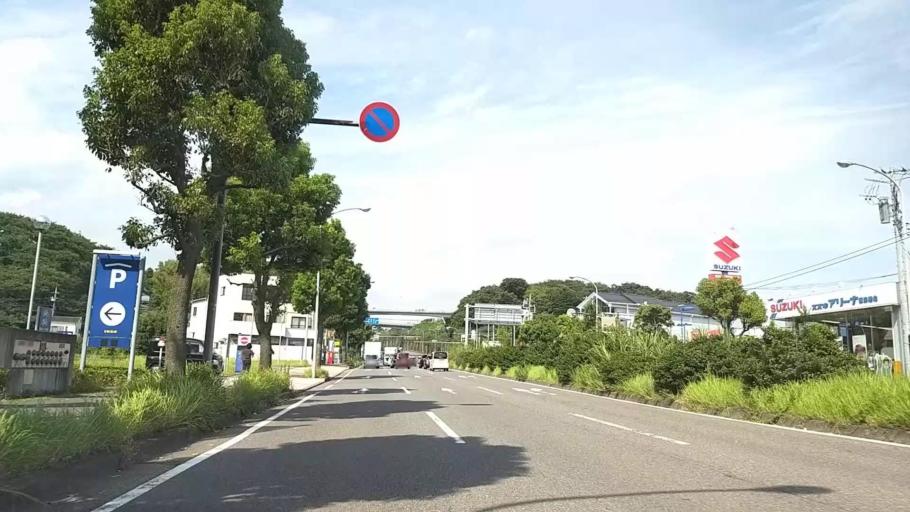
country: JP
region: Kanagawa
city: Yokohama
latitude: 35.5229
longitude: 139.5912
